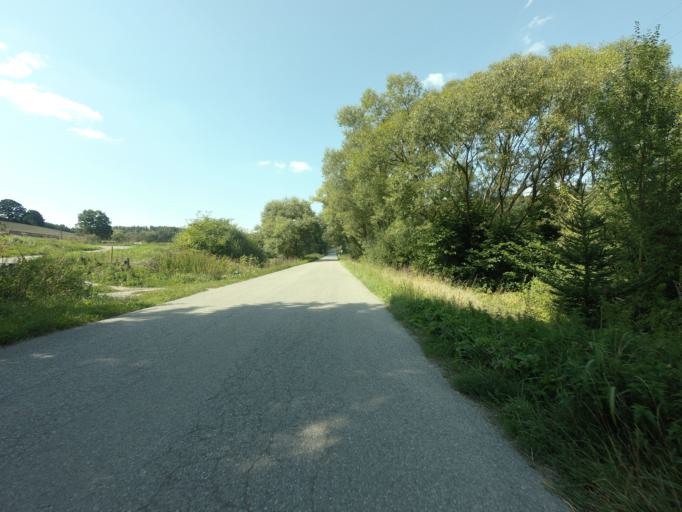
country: CZ
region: Jihocesky
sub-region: Okres Ceske Budejovice
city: Hluboka nad Vltavou
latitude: 49.1349
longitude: 14.4494
